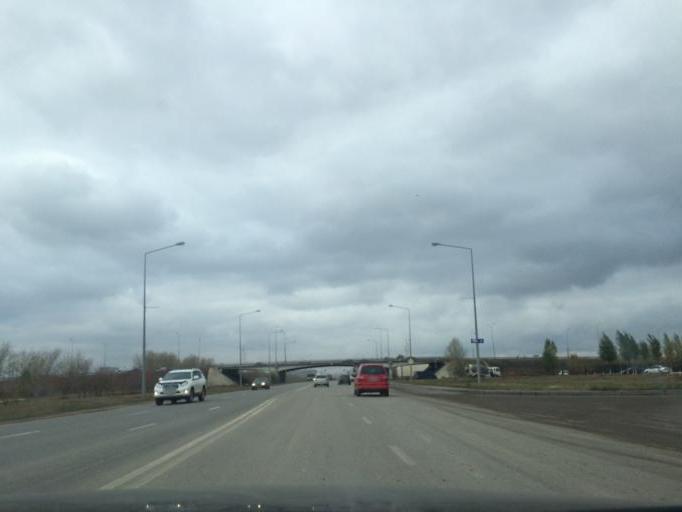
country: KZ
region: Astana Qalasy
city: Astana
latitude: 51.1388
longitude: 71.5273
